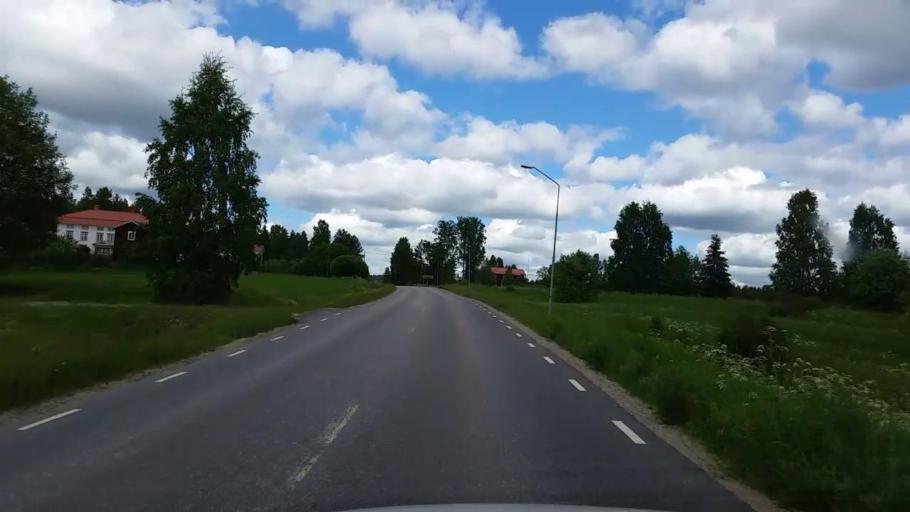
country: SE
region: Gaevleborg
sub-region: Ovanakers Kommun
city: Alfta
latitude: 61.3967
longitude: 16.0462
